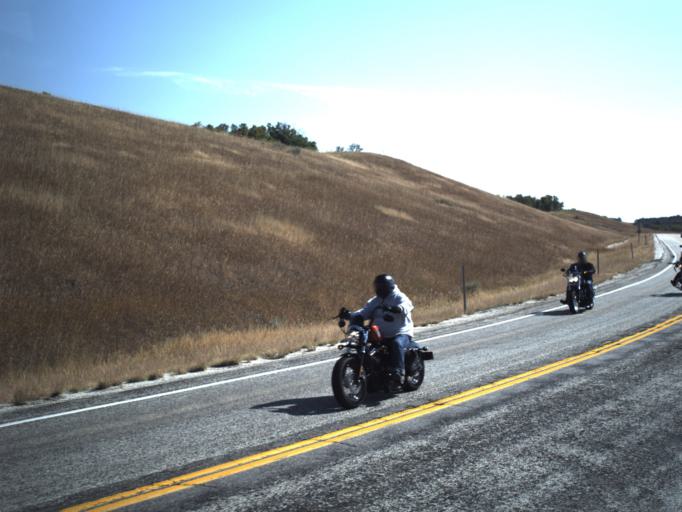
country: US
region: Utah
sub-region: Morgan County
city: Mountain Green
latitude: 41.2279
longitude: -111.7906
